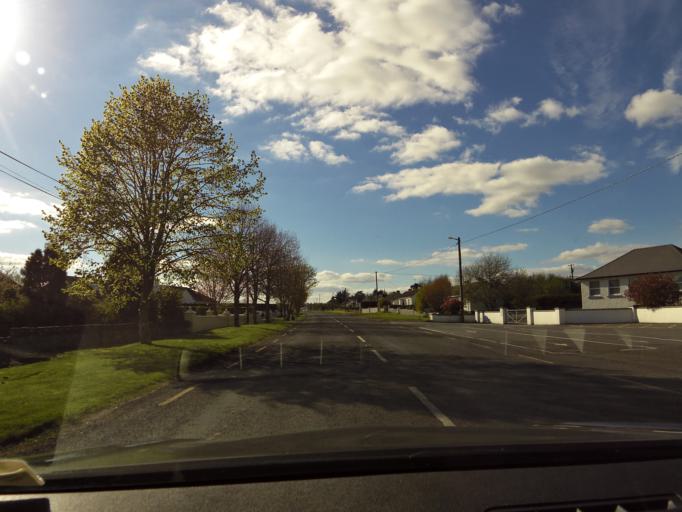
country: IE
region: Leinster
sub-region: Uibh Fhaili
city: Birr
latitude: 53.0889
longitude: -7.9385
